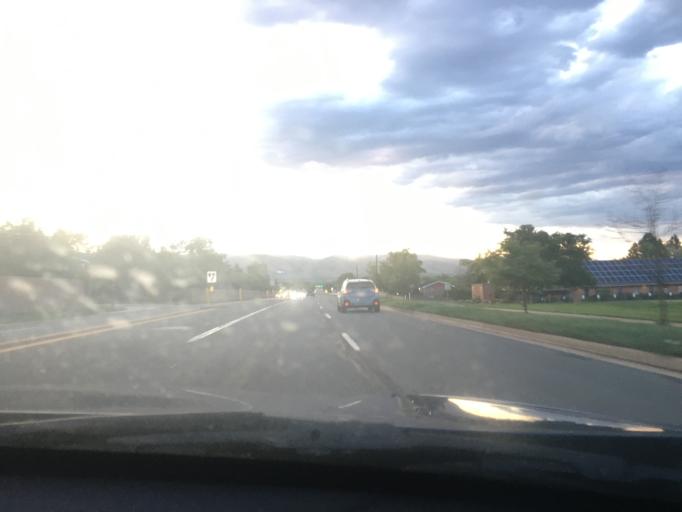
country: US
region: Colorado
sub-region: Boulder County
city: Boulder
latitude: 39.9772
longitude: -105.2423
